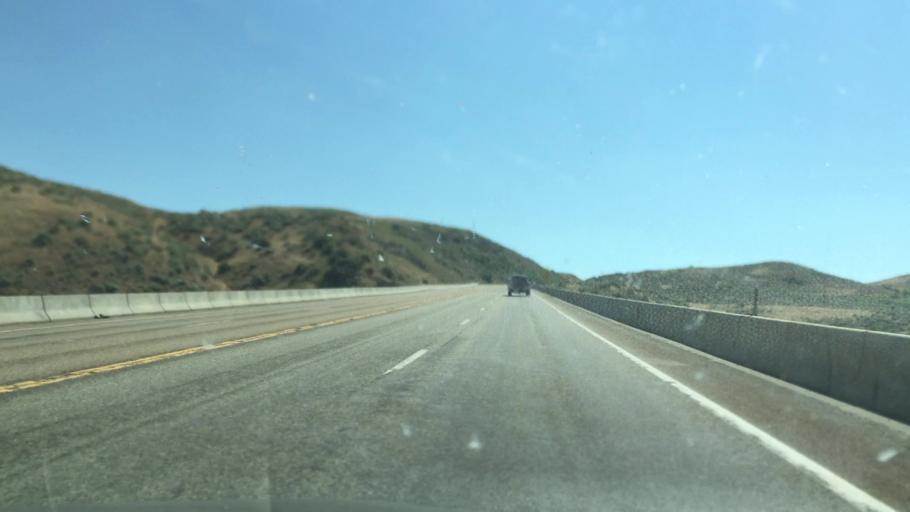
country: US
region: Idaho
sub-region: Ada County
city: Eagle
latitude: 43.8411
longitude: -116.2356
